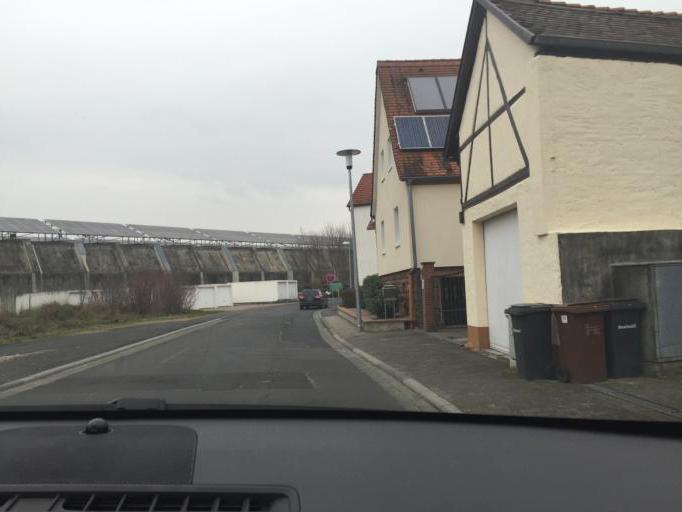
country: DE
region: Bavaria
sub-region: Regierungsbezirk Unterfranken
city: Hosbach
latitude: 49.9987
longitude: 9.2019
